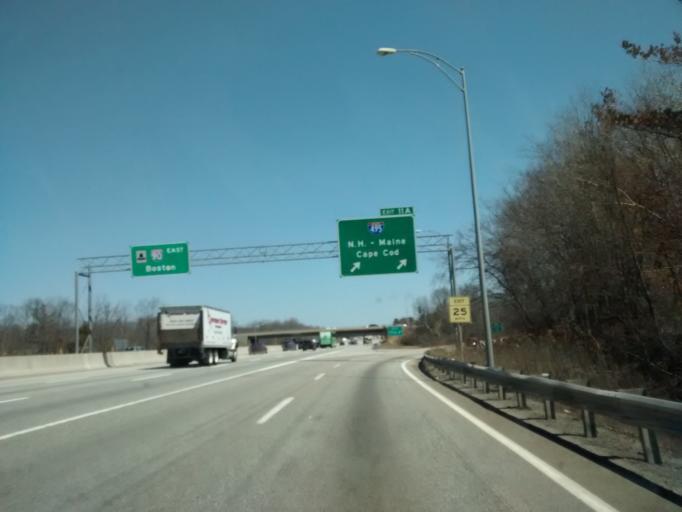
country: US
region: Massachusetts
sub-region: Worcester County
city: Westborough
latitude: 42.2632
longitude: -71.5720
